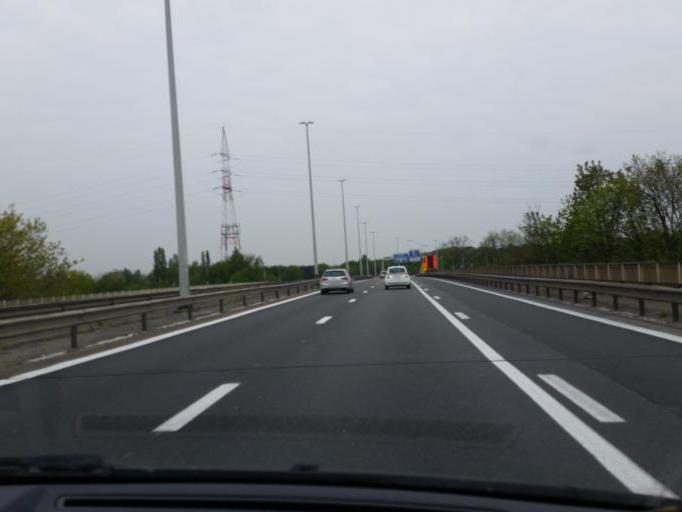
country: BE
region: Flanders
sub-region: Provincie Oost-Vlaanderen
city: Merelbeke
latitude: 51.0043
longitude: 3.7696
